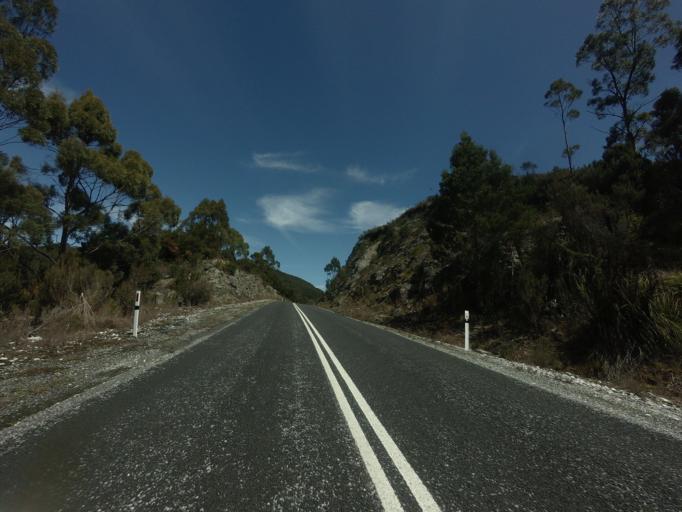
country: AU
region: Tasmania
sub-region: West Coast
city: Queenstown
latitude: -42.7952
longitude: 146.0833
